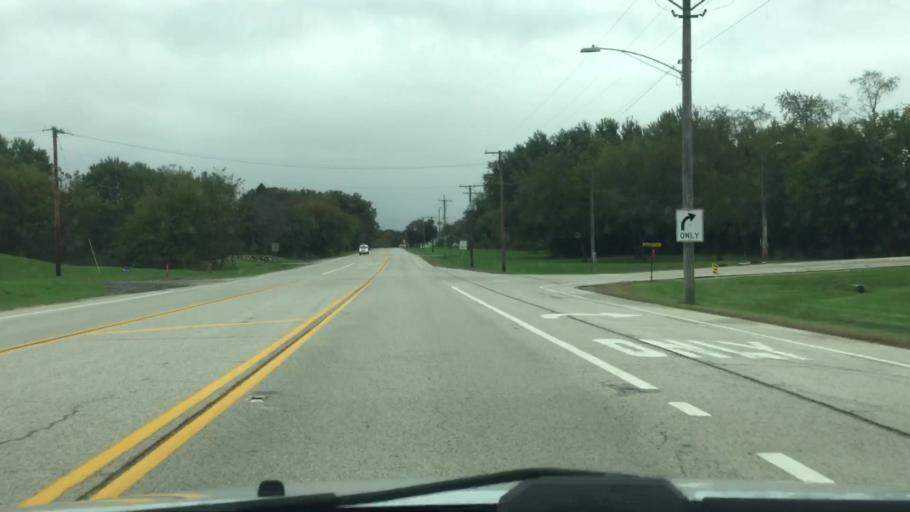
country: US
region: Illinois
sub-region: McHenry County
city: Richmond
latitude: 42.4451
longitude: -88.3059
